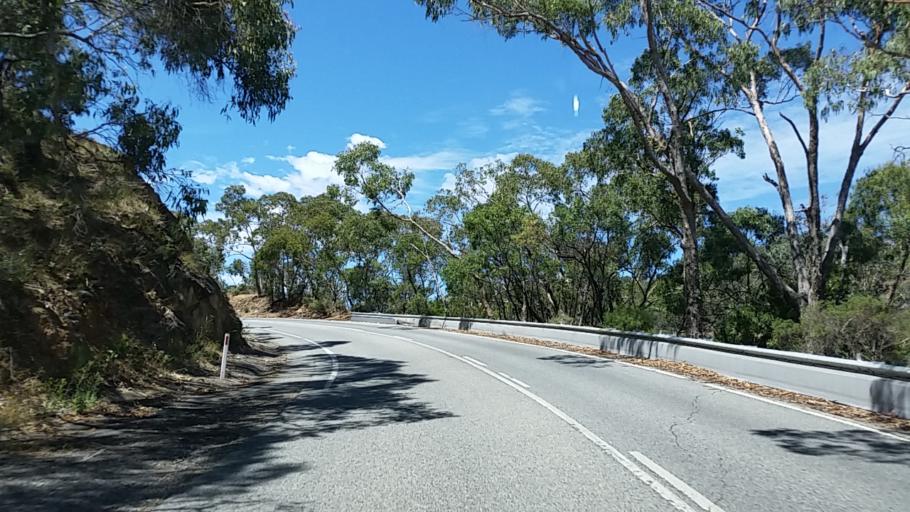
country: AU
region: South Australia
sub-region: Campbelltown
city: Athelstone
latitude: -34.8640
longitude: 138.7834
